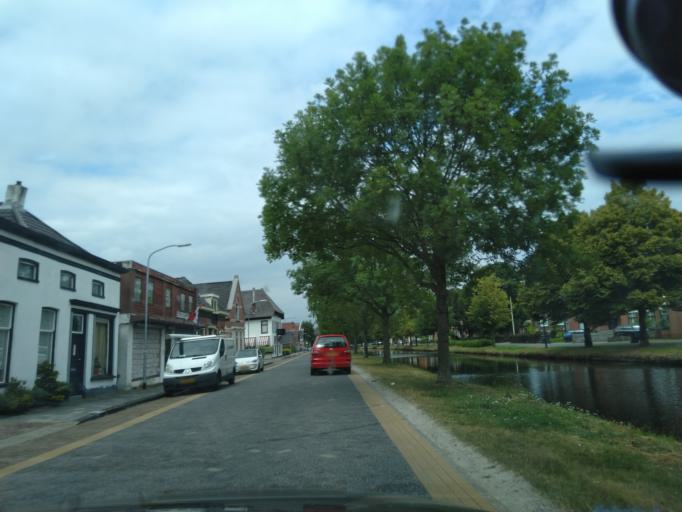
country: NL
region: Groningen
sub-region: Gemeente Pekela
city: Oude Pekela
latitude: 53.0954
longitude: 6.9909
